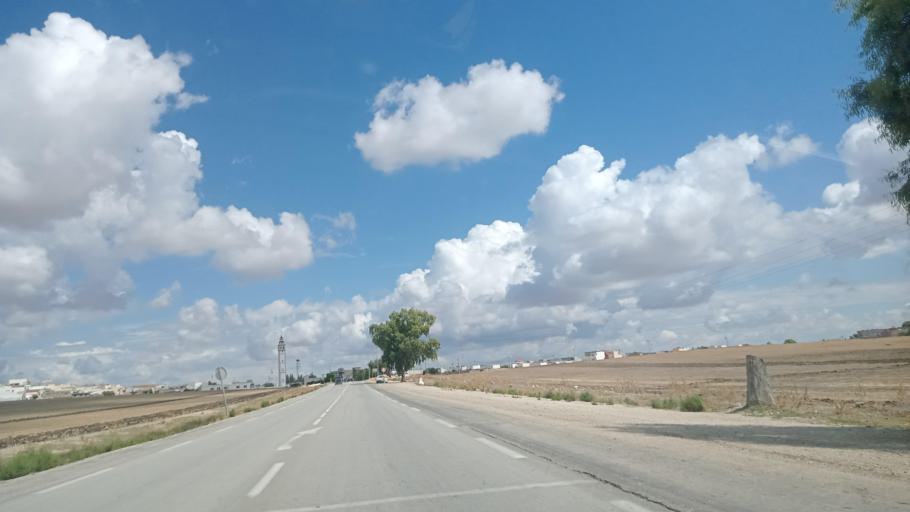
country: TN
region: Silyanah
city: Al Karib
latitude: 36.3219
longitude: 9.1267
